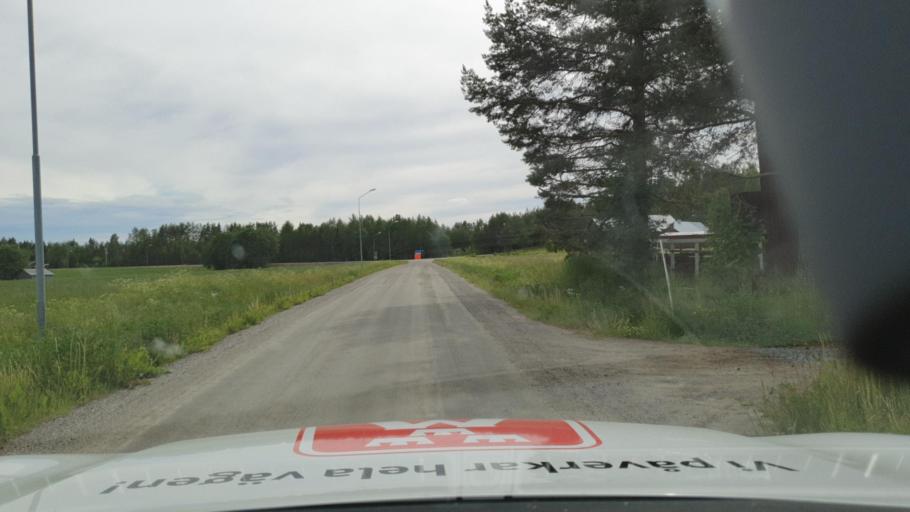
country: SE
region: Vaesterbotten
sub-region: Robertsfors Kommun
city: Robertsfors
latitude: 64.4139
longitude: 21.0025
